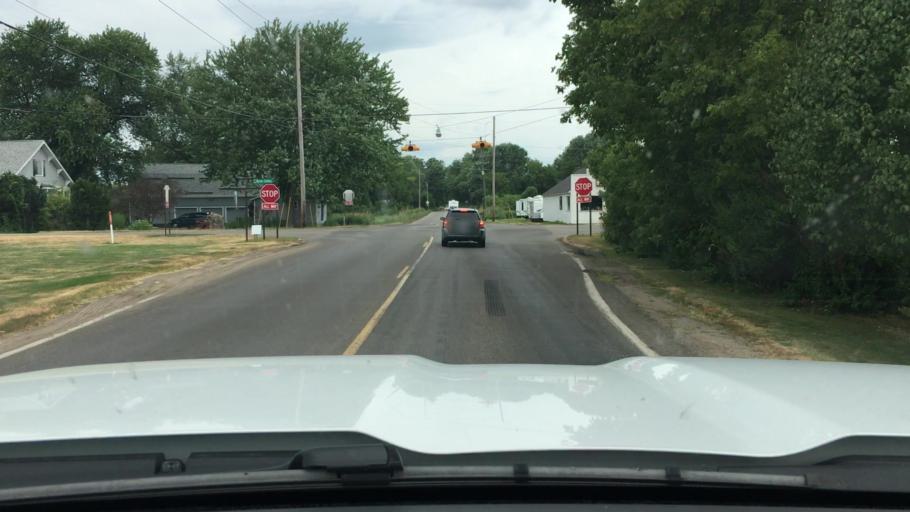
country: US
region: Michigan
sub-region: Kent County
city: Byron Center
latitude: 42.7830
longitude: -85.7221
